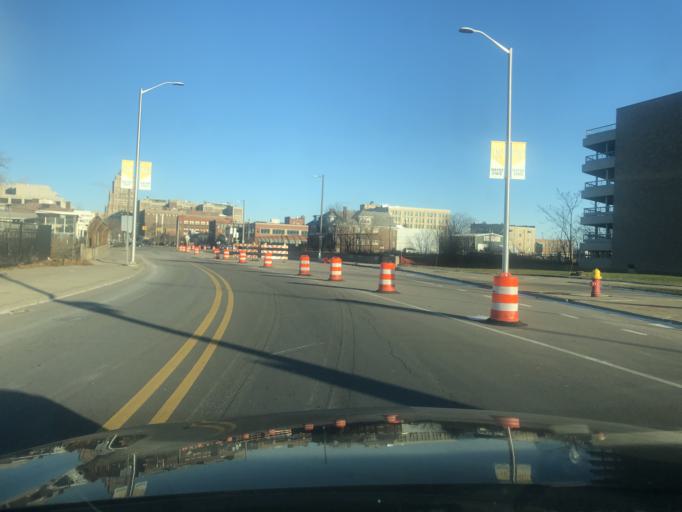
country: US
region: Michigan
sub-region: Wayne County
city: Hamtramck
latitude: 42.3609
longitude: -83.0722
